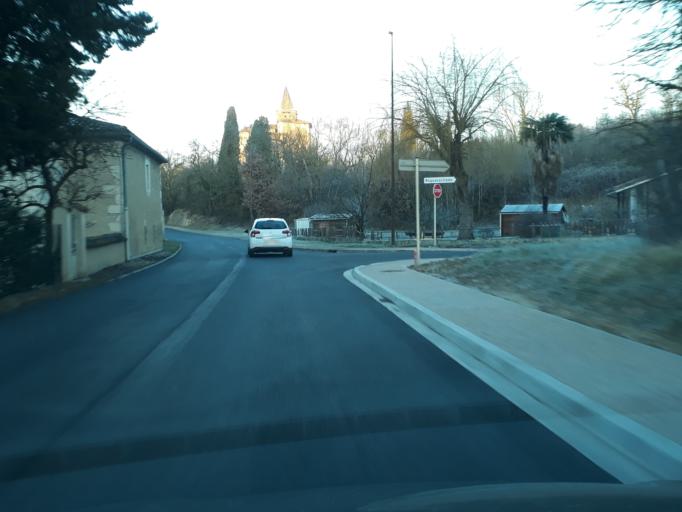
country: FR
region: Midi-Pyrenees
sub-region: Departement du Gers
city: Pavie
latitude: 43.6205
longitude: 0.6521
